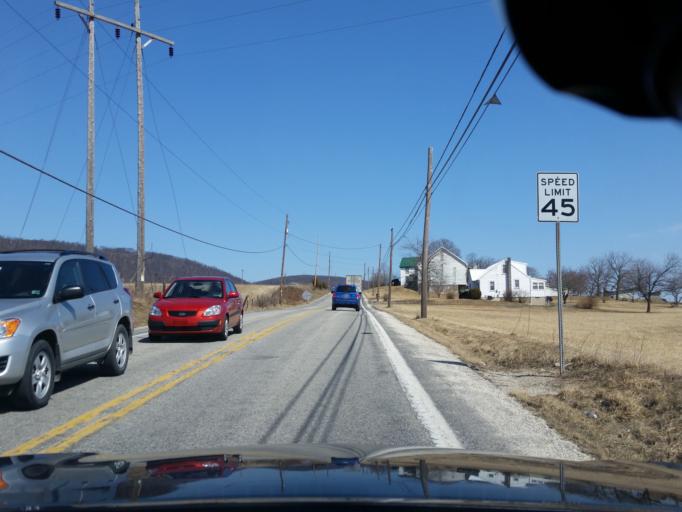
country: US
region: Pennsylvania
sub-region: Cumberland County
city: Schlusser
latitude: 40.2734
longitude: -77.1615
